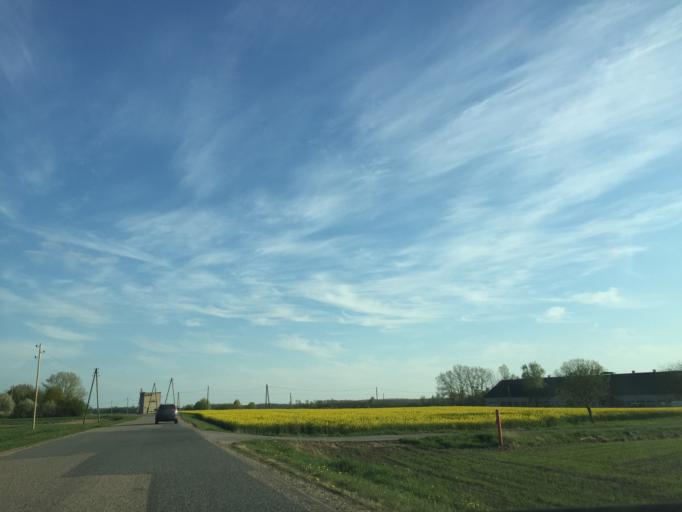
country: LV
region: Bauskas Rajons
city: Bauska
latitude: 56.2990
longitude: 24.2610
